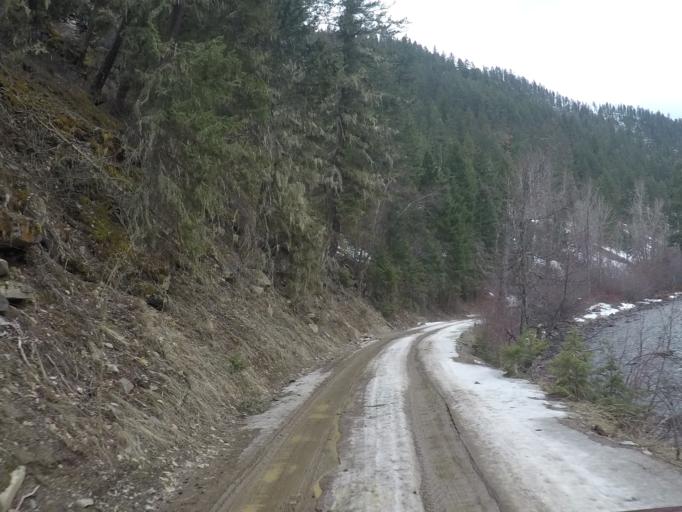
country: US
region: Montana
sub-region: Missoula County
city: Clinton
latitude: 46.5700
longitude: -113.6867
